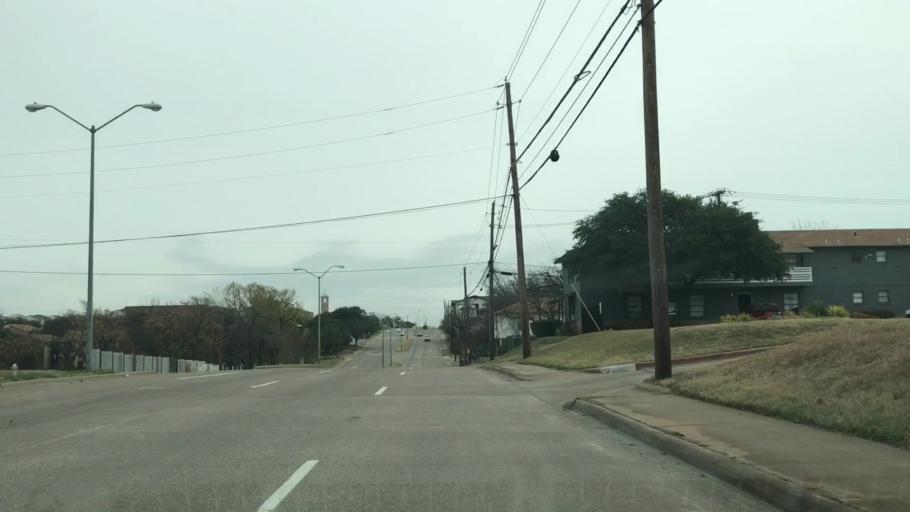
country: US
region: Texas
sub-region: Dallas County
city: Cockrell Hill
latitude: 32.7495
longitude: -96.8551
